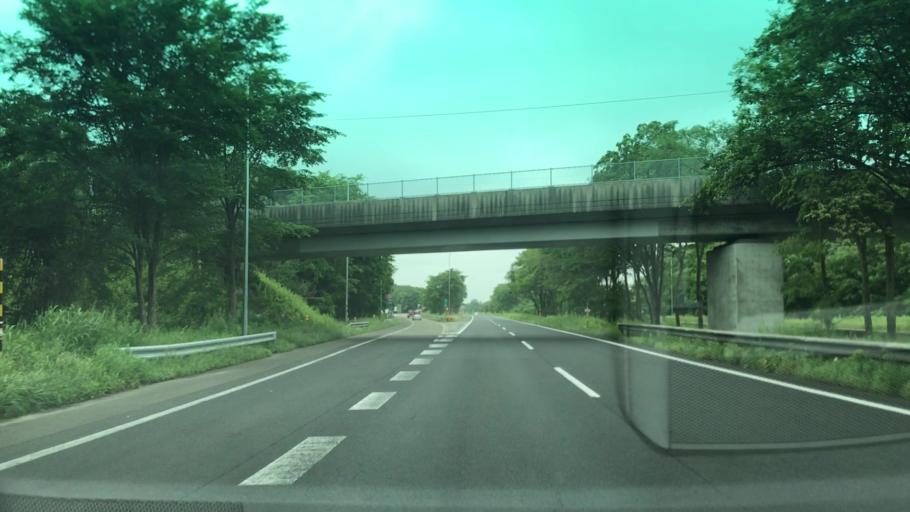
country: JP
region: Hokkaido
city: Chitose
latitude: 42.7539
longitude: 141.6436
